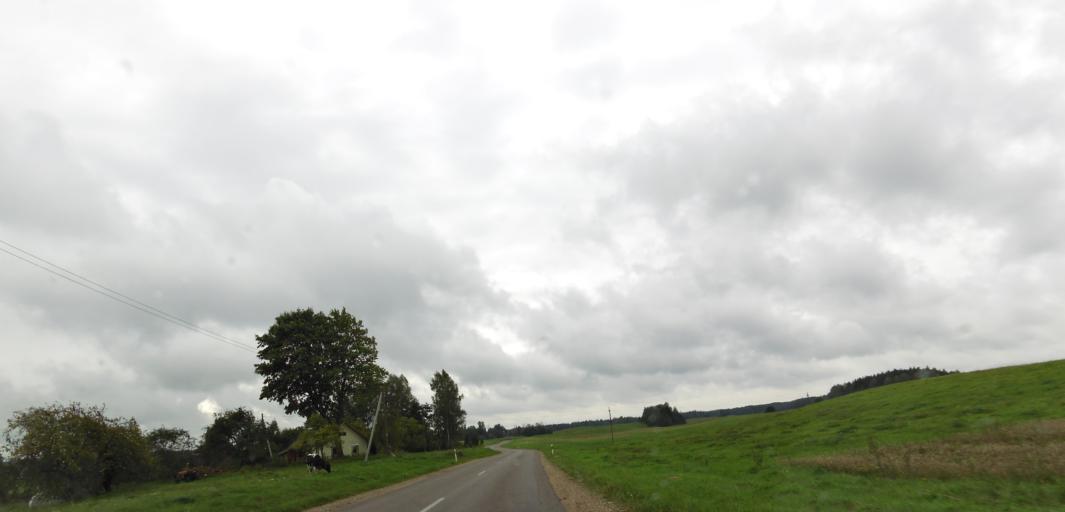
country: LT
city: Moletai
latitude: 55.3019
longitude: 25.3434
